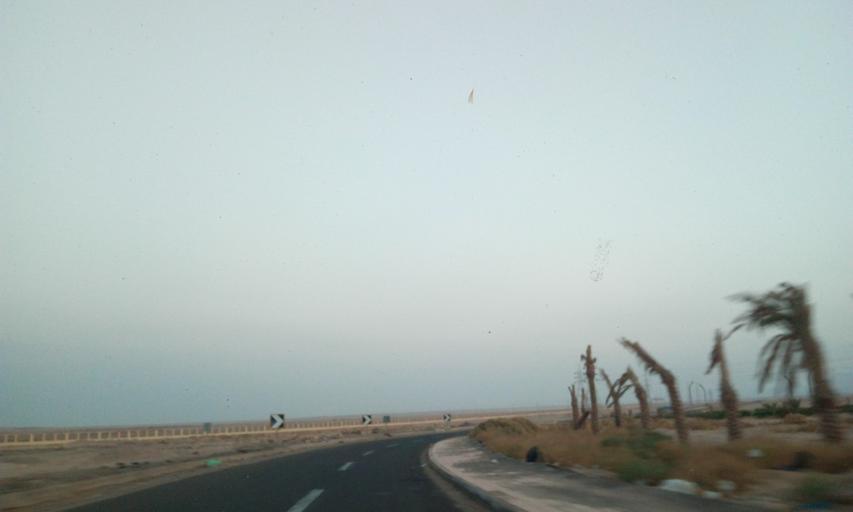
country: EG
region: Red Sea
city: El Gouna
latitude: 27.3288
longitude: 33.6660
